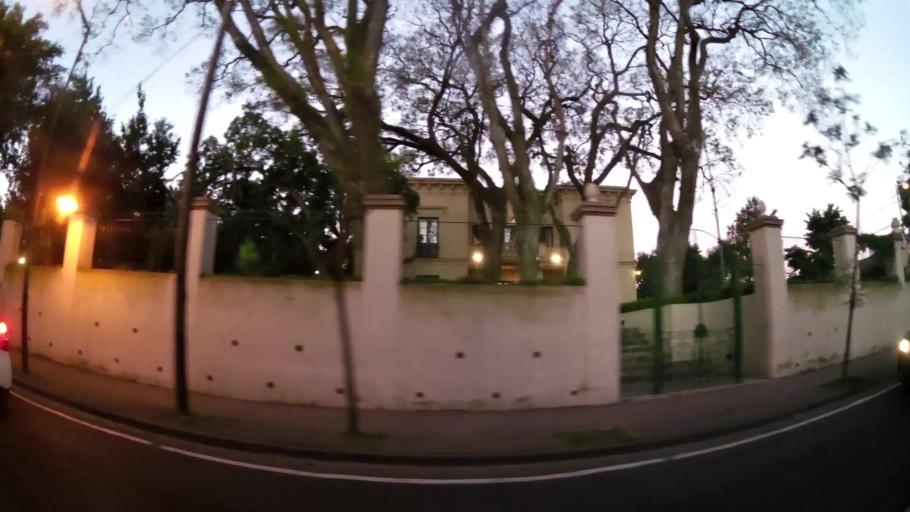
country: AR
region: Buenos Aires
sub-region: Partido de Tigre
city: Tigre
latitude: -34.4367
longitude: -58.5591
